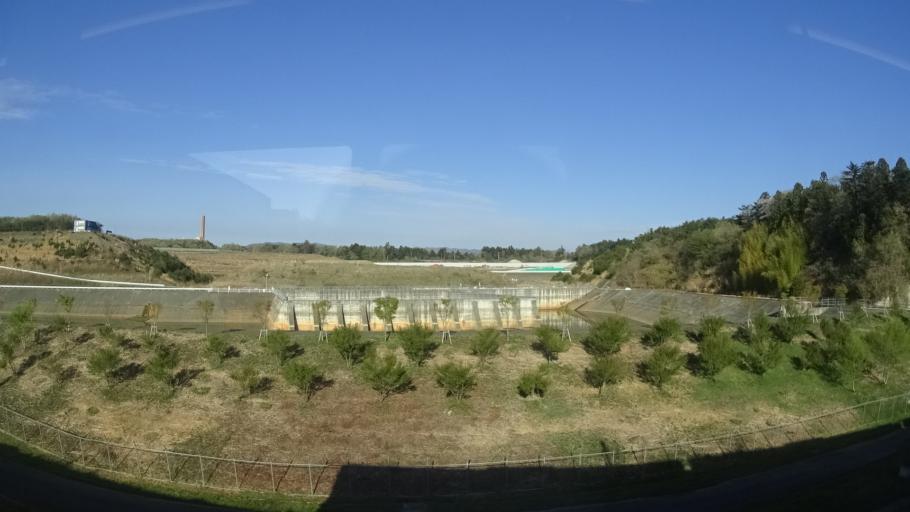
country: JP
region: Fukushima
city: Namie
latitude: 37.6735
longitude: 140.9719
